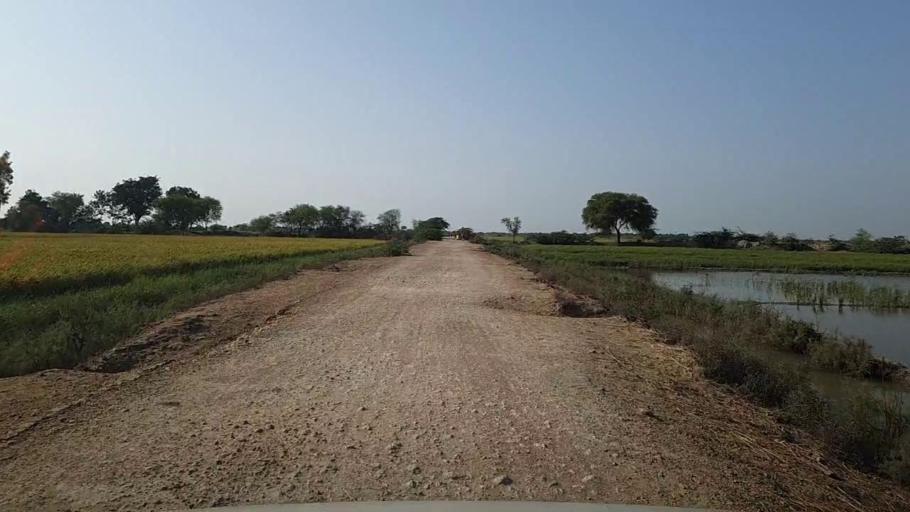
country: PK
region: Sindh
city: Kario
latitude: 24.8063
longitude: 68.5105
